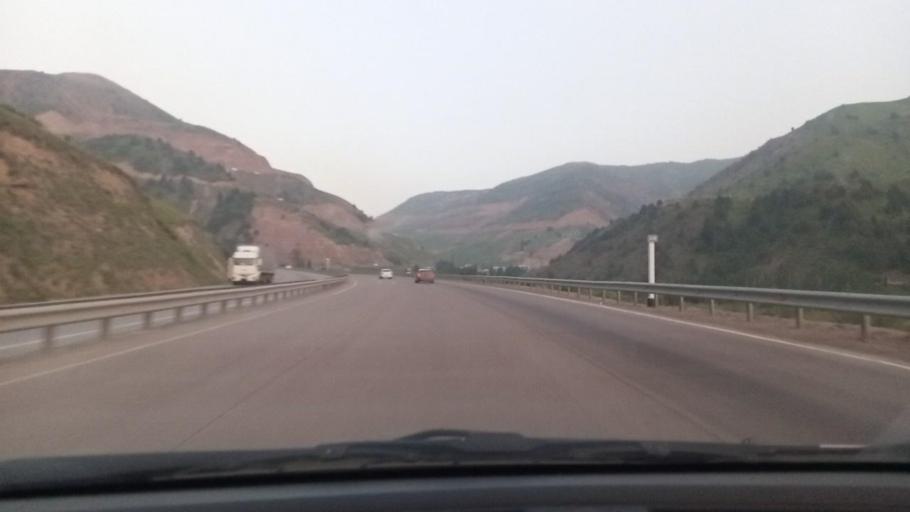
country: UZ
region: Toshkent
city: Angren
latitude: 41.1197
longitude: 70.4895
